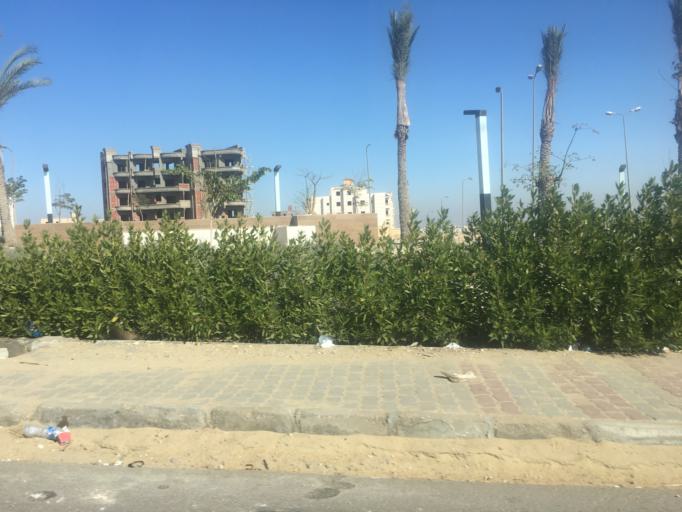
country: EG
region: Al Jizah
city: Awsim
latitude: 30.0121
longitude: 30.9792
